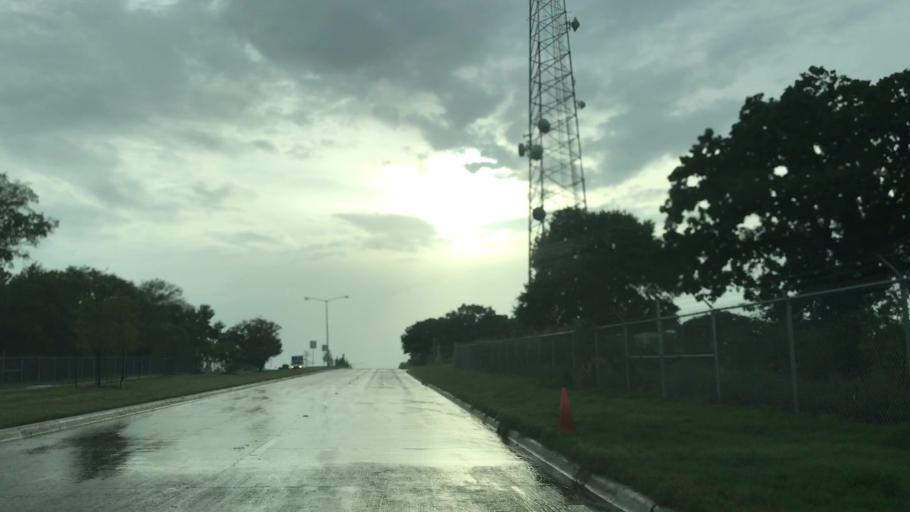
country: US
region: Texas
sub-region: Denton County
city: Lewisville
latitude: 33.0569
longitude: -96.9872
